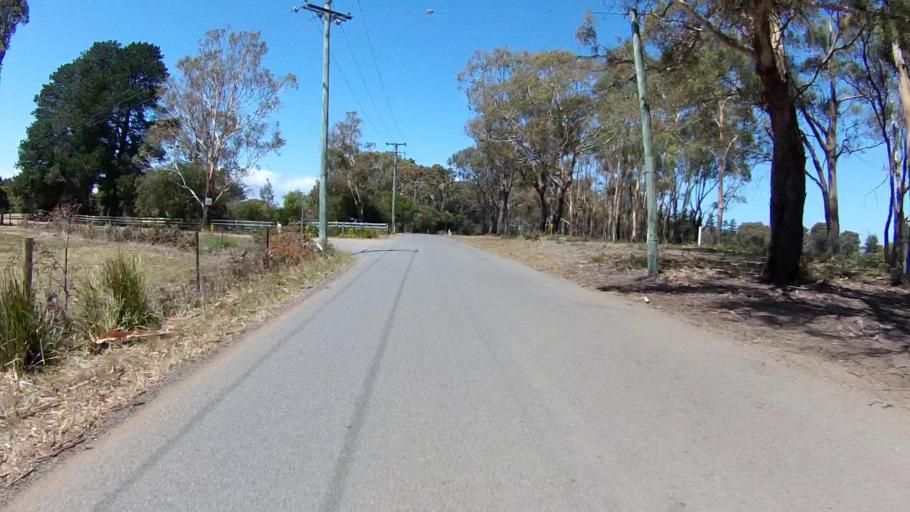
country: AU
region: Tasmania
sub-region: Clarence
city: Sandford
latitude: -42.9302
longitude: 147.4967
